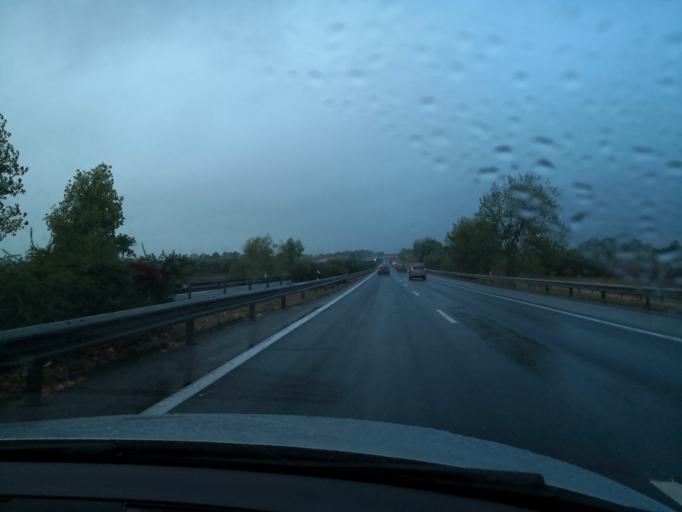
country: PT
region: Setubal
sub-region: Moita
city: Moita
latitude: 38.6540
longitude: -8.9658
